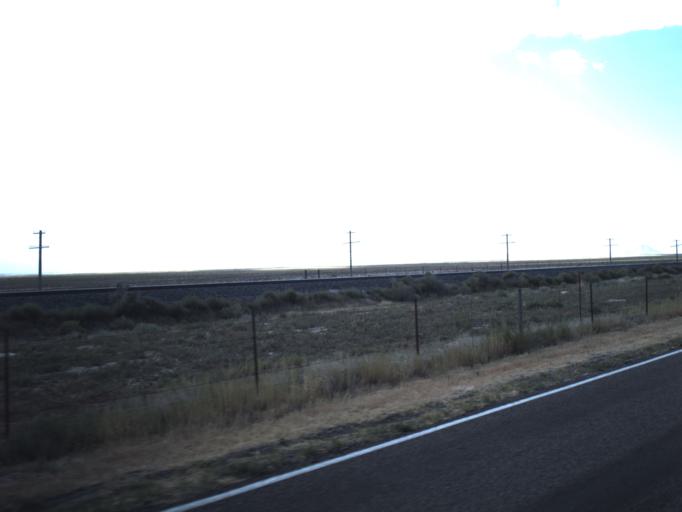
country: US
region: Utah
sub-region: Millard County
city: Delta
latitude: 39.0205
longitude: -112.7794
